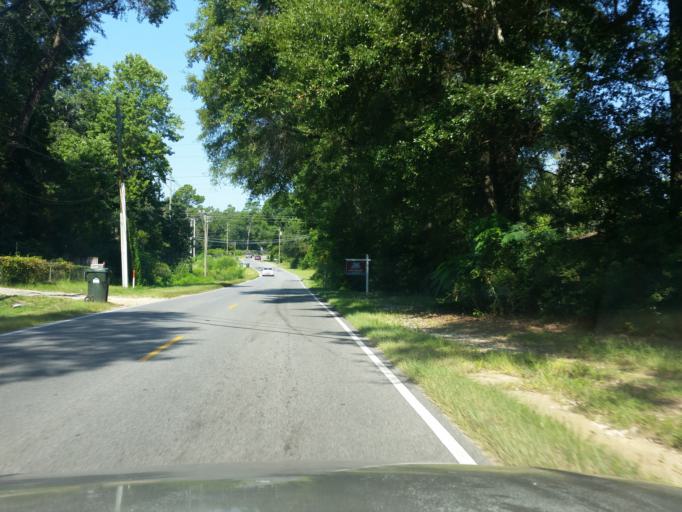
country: US
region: Florida
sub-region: Escambia County
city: Ensley
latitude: 30.5174
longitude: -87.2425
